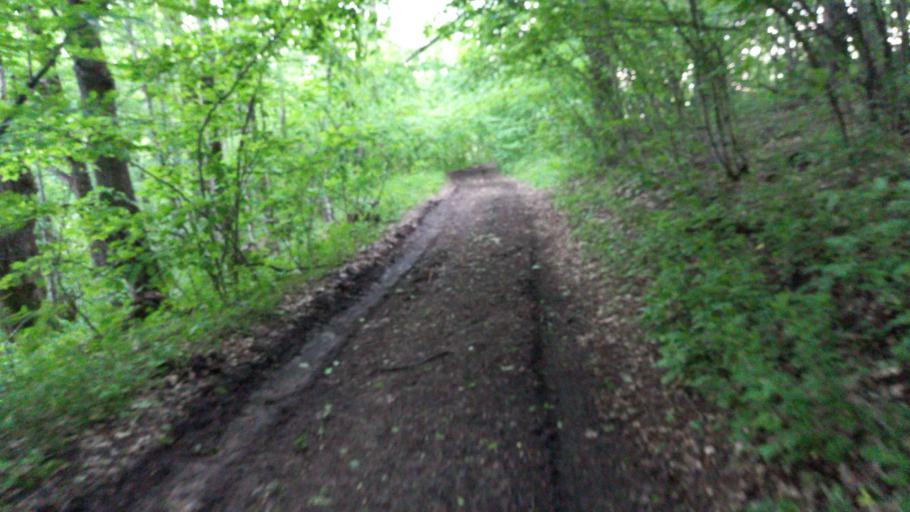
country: RU
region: Adygeya
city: Kamennomostskiy
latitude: 44.2169
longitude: 39.9923
